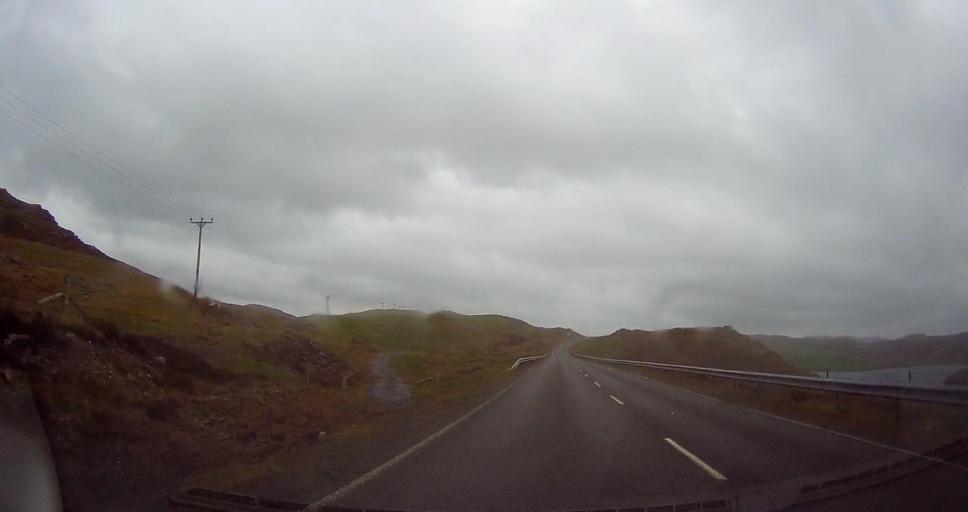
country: GB
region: Scotland
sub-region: Shetland Islands
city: Lerwick
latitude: 60.4232
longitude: -1.3952
